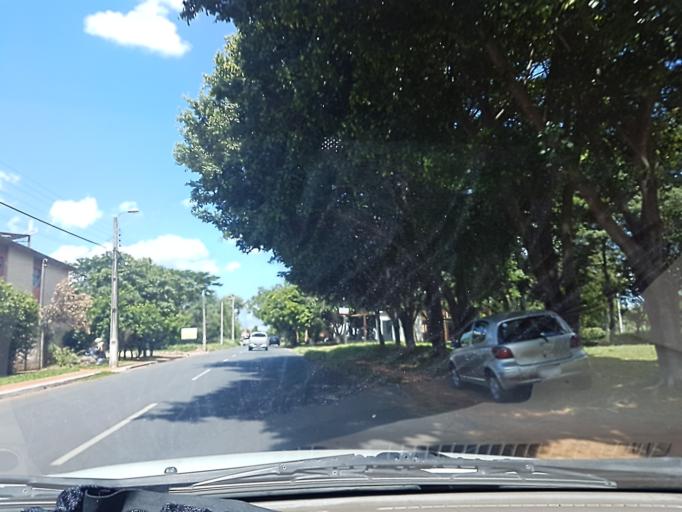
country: PY
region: Central
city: Fernando de la Mora
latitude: -25.2586
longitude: -57.5096
